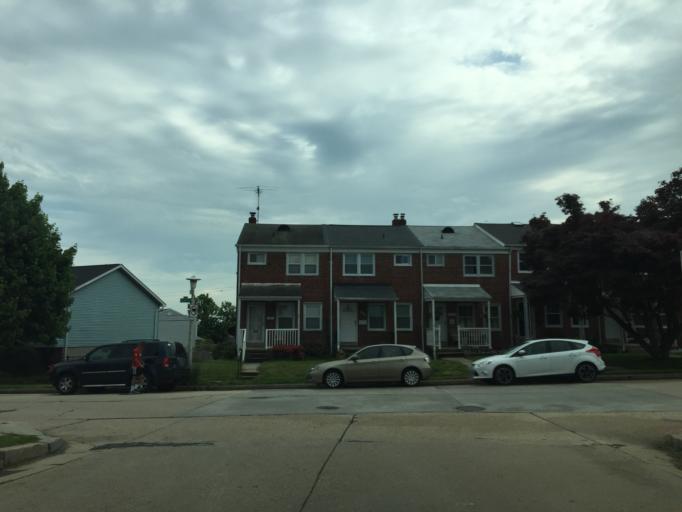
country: US
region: Maryland
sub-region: City of Baltimore
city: Baltimore
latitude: 39.3400
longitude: -76.6405
